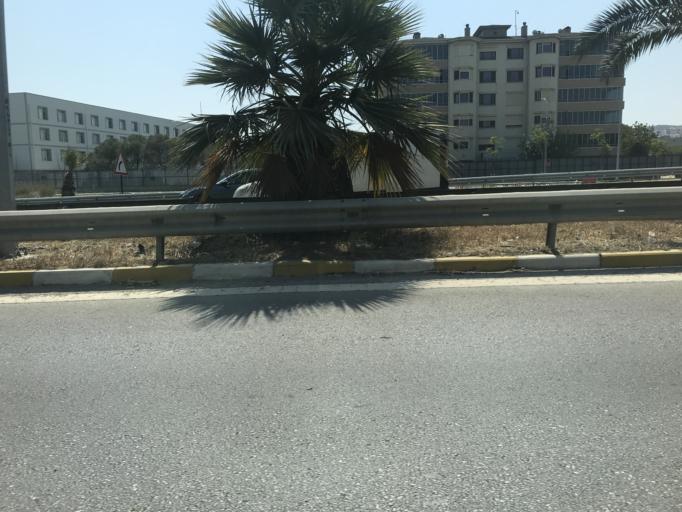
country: TR
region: Izmir
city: Karsiyaka
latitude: 38.4024
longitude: 27.0690
